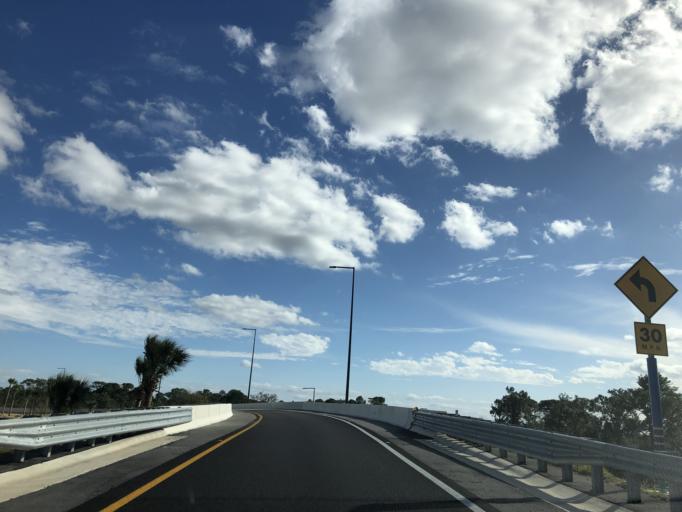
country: US
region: Florida
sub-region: Osceola County
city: Celebration
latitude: 28.3467
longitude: -81.5539
